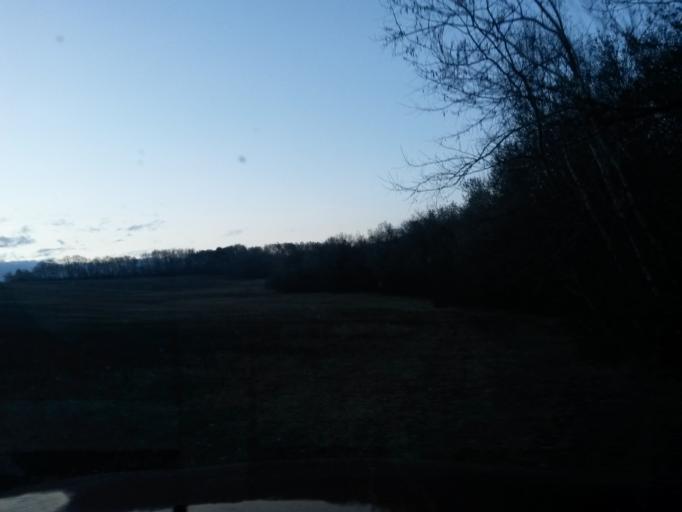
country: SK
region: Kosicky
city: Kosice
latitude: 48.7030
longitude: 21.3119
